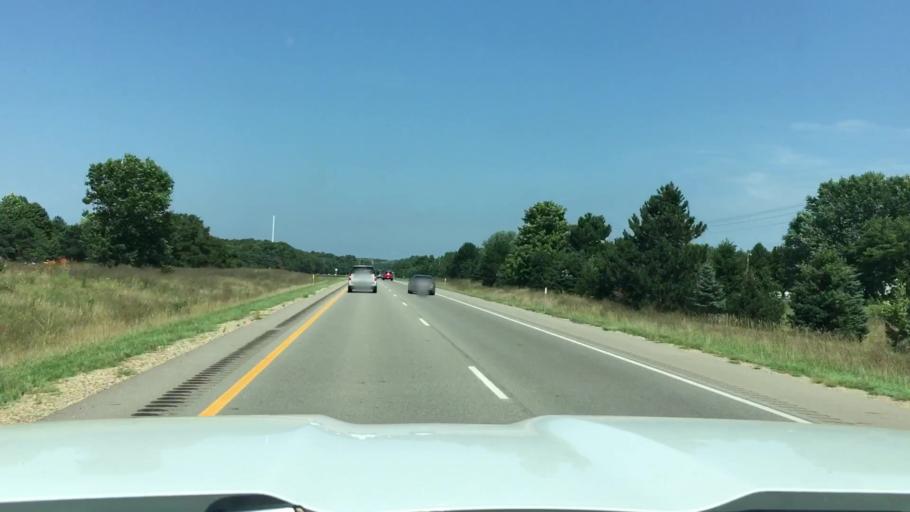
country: US
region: Michigan
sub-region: Kalamazoo County
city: Portage
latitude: 42.1876
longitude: -85.6460
